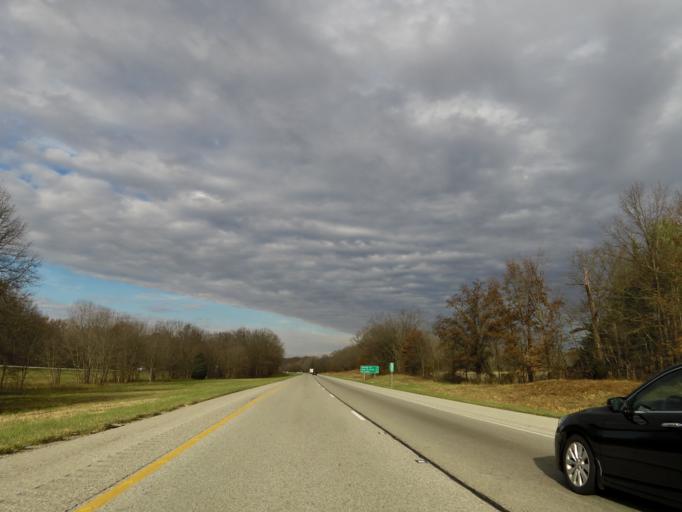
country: US
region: Illinois
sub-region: Washington County
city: Nashville
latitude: 38.3955
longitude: -89.3874
